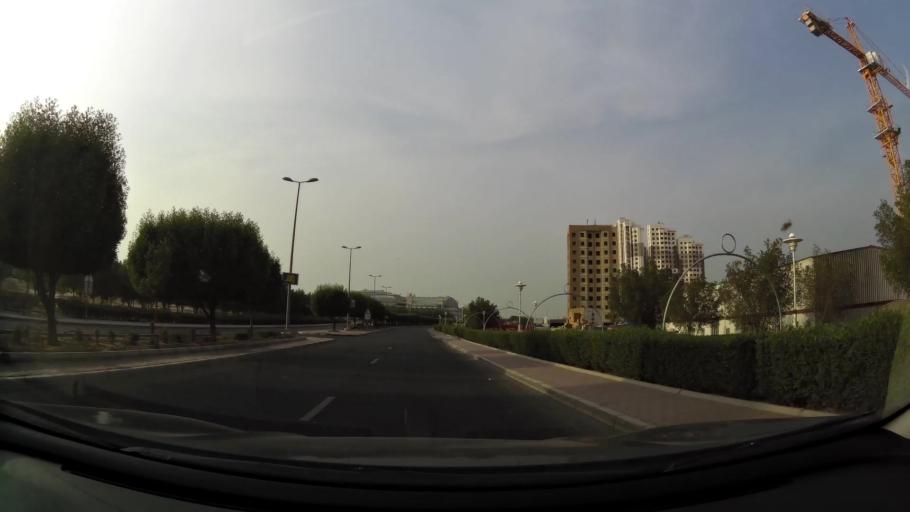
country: KW
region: Mubarak al Kabir
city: Sabah as Salim
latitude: 29.2617
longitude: 48.0781
